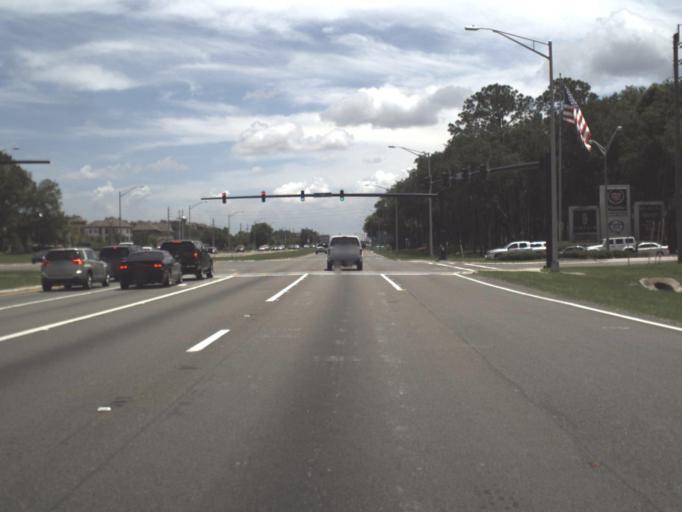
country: US
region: Florida
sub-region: Duval County
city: Jacksonville
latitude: 30.2607
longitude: -81.5566
